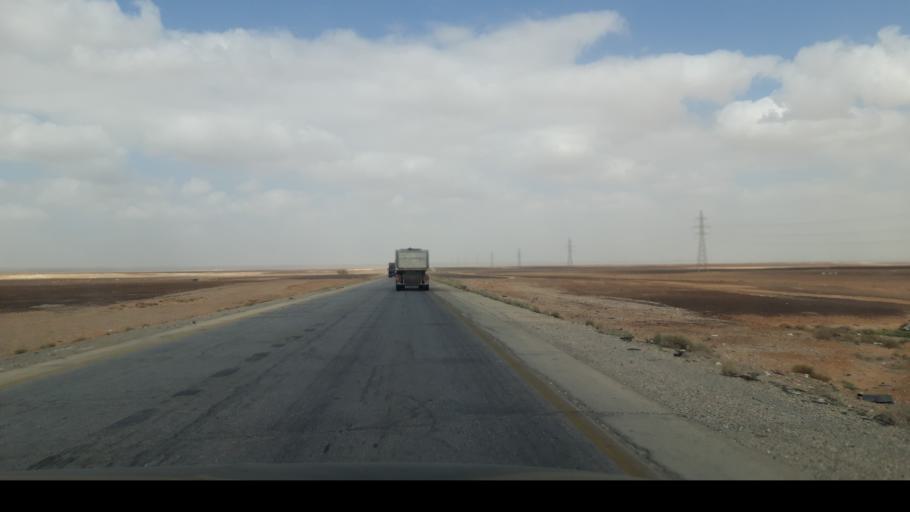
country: JO
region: Amman
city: Al Azraq ash Shamali
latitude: 31.7725
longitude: 36.5651
